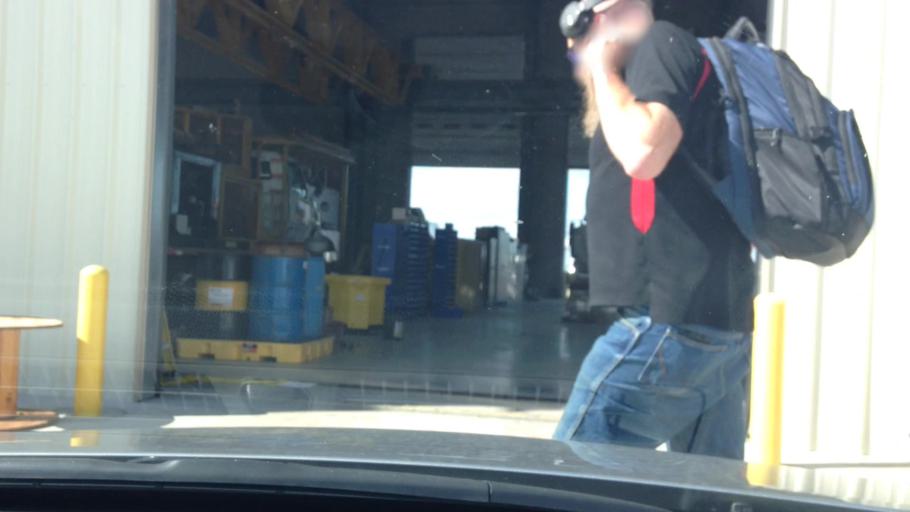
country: US
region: Missouri
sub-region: Clay County
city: Smithville
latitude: 39.3412
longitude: -94.6606
